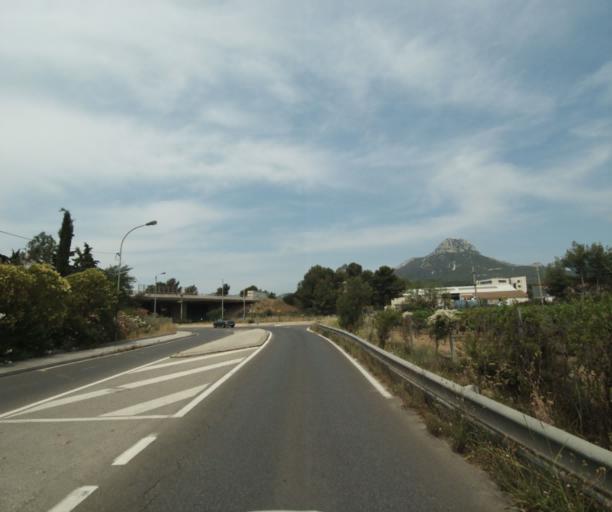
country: FR
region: Provence-Alpes-Cote d'Azur
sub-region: Departement du Var
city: La Farlede
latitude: 43.1402
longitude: 6.0396
